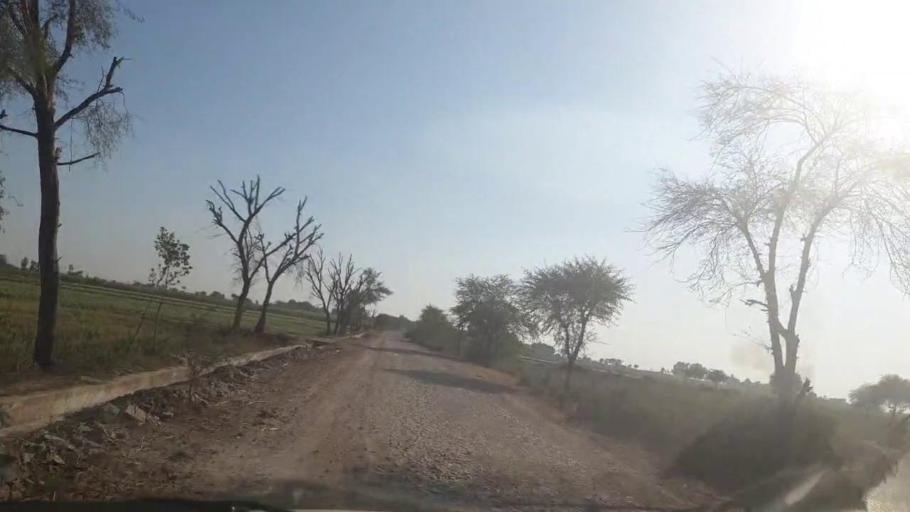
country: PK
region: Sindh
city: Mirwah Gorchani
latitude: 25.4273
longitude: 69.1661
